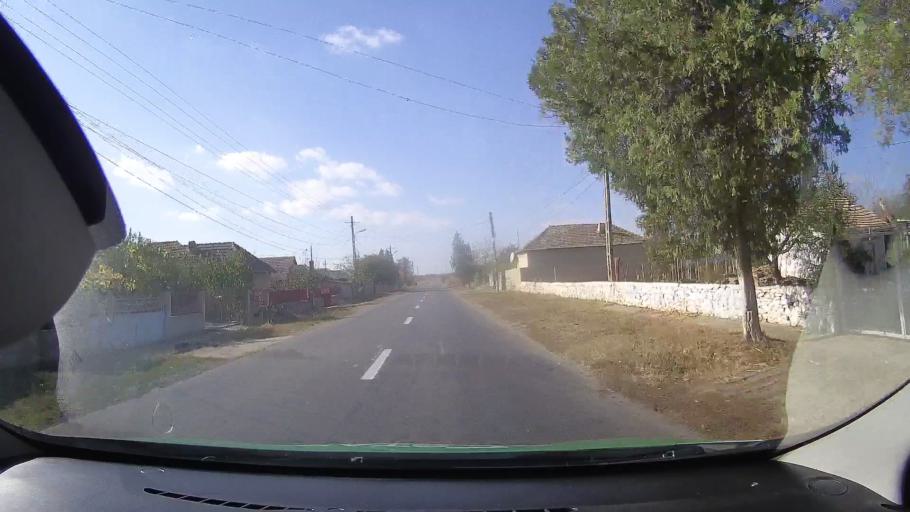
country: RO
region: Constanta
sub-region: Comuna Cogealac
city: Tariverde
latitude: 44.5617
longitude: 28.5866
